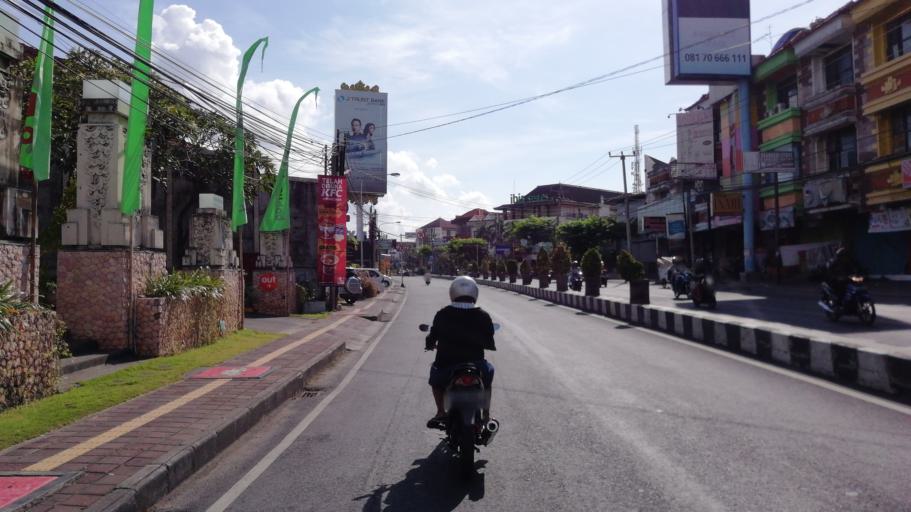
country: ID
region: Bali
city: Karyadharma
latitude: -8.6799
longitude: 115.2039
